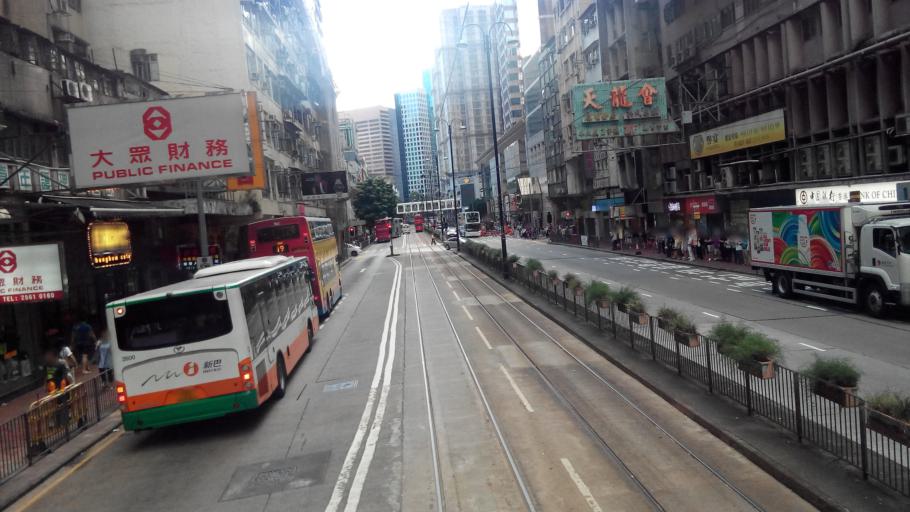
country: HK
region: Wanchai
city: Wan Chai
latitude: 22.2913
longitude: 114.2003
